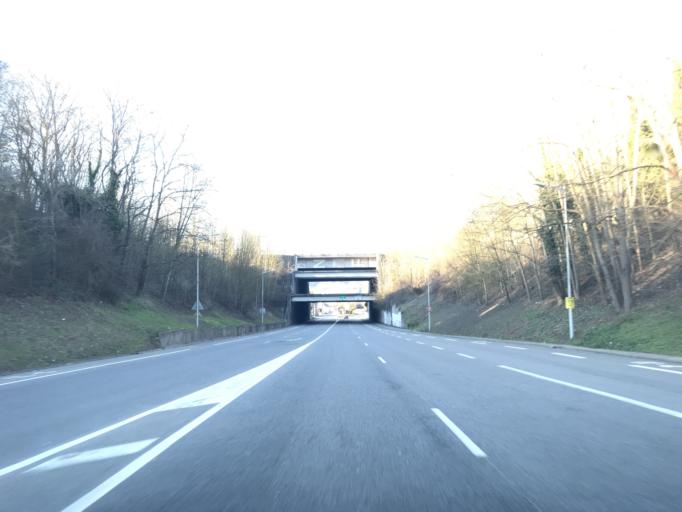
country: FR
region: Haute-Normandie
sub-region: Departement de l'Eure
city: Evreux
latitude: 49.0159
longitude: 1.1442
